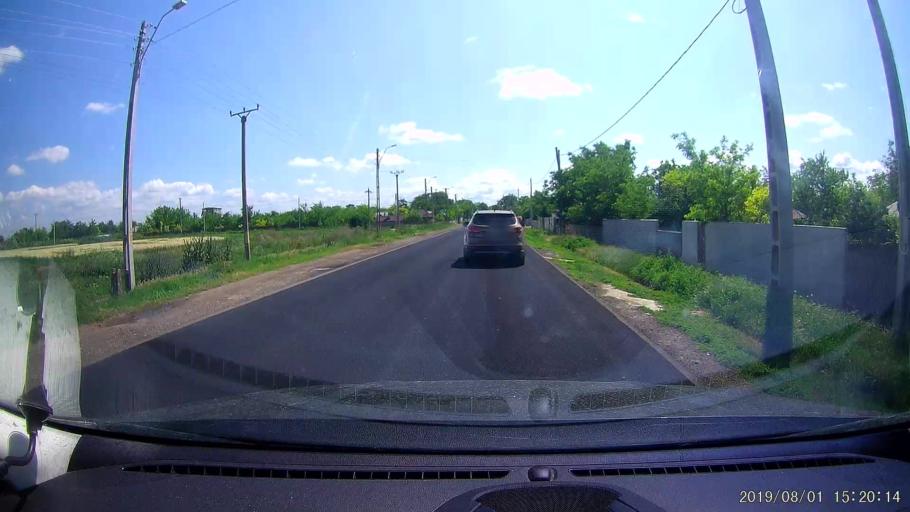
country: RO
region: Braila
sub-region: Comuna Tufesti
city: Tufesti
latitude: 45.0810
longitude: 27.8081
